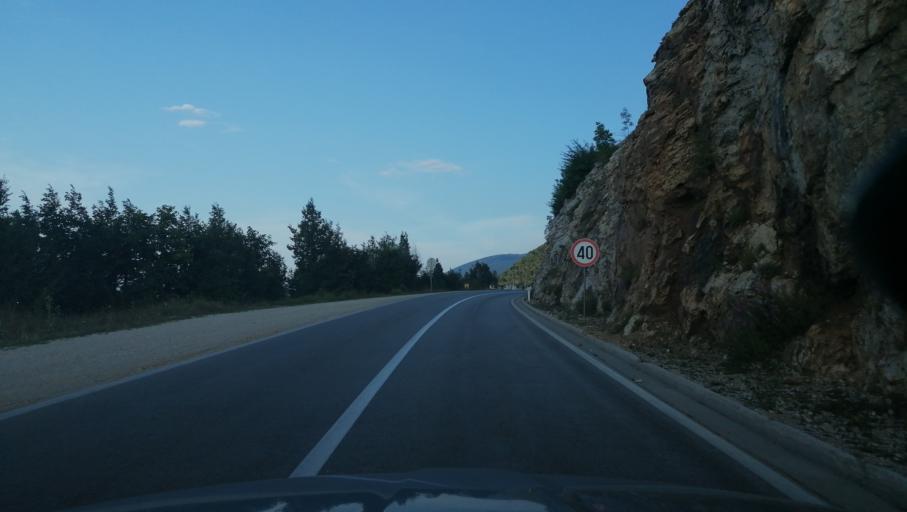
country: BA
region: Federation of Bosnia and Herzegovina
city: Prozor
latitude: 43.8384
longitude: 17.5837
